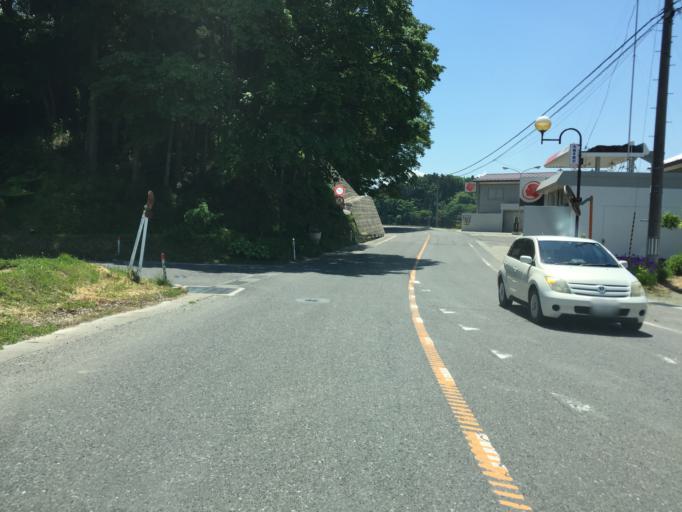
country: JP
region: Fukushima
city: Motomiya
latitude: 37.5023
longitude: 140.4576
